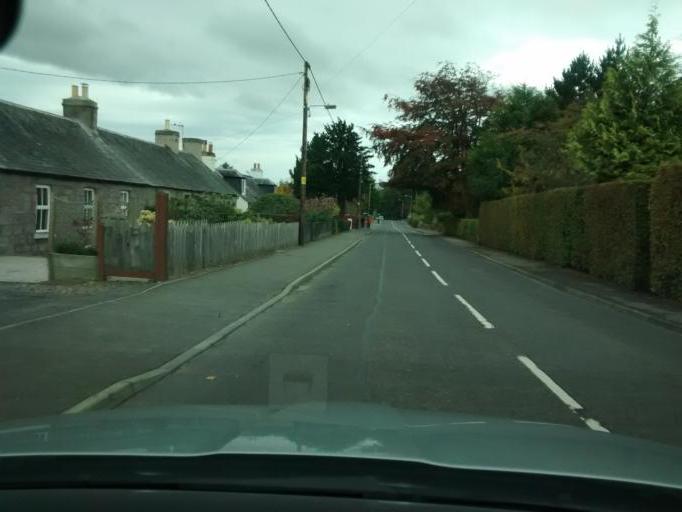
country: GB
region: Scotland
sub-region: Perth and Kinross
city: Stanley
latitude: 56.4841
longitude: -3.4518
